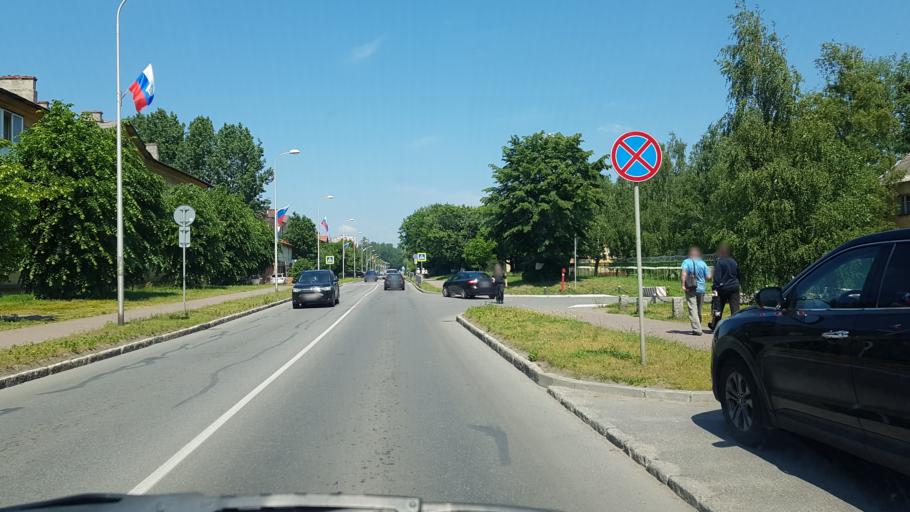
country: RU
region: Kaliningrad
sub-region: Gorod Kaliningrad
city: Baltiysk
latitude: 54.6565
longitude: 19.9127
